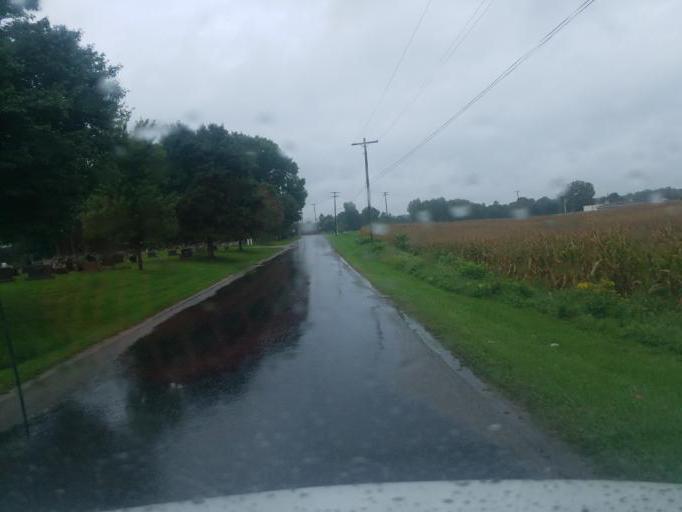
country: US
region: Ohio
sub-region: Wayne County
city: Creston
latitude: 40.9860
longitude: -81.9012
